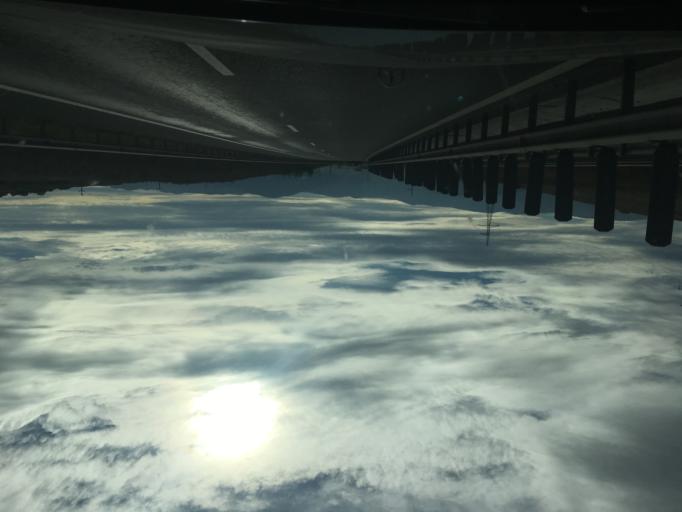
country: RO
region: Sibiu
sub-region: Comuna Cristian
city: Cristian
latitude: 45.7968
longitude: 24.0245
